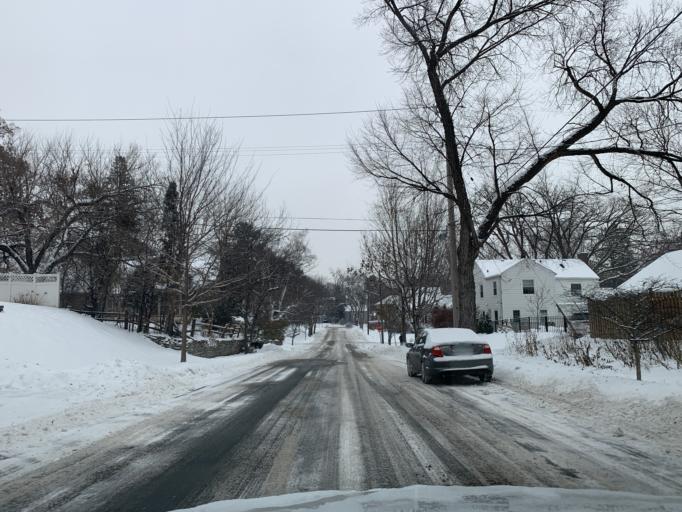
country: US
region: Minnesota
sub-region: Hennepin County
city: Saint Louis Park
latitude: 44.9521
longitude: -93.3311
